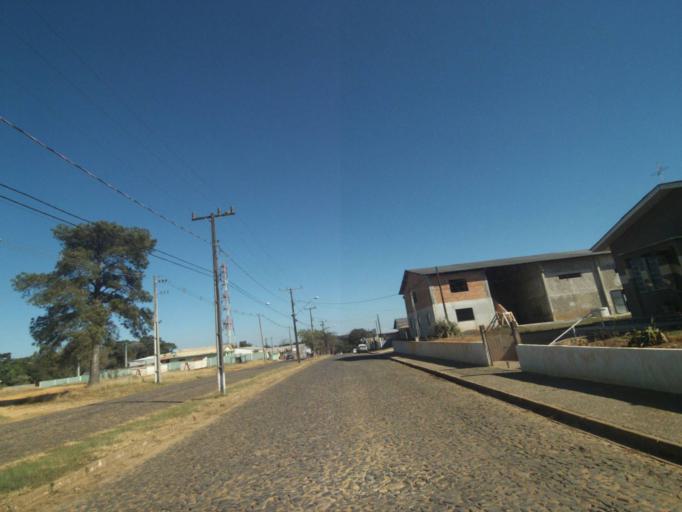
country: BR
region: Parana
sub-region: Reserva
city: Reserva
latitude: -24.6250
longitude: -50.6421
